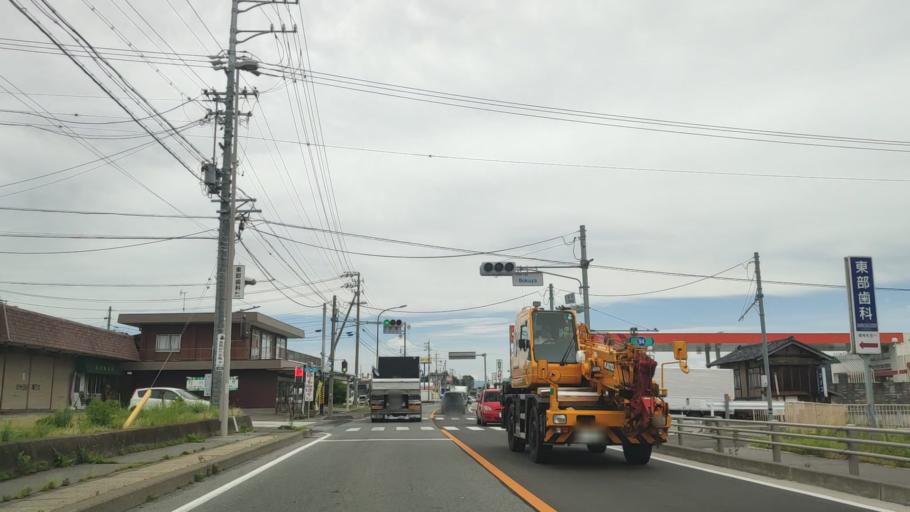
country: JP
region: Nagano
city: Komoro
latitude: 36.3487
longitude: 138.3654
